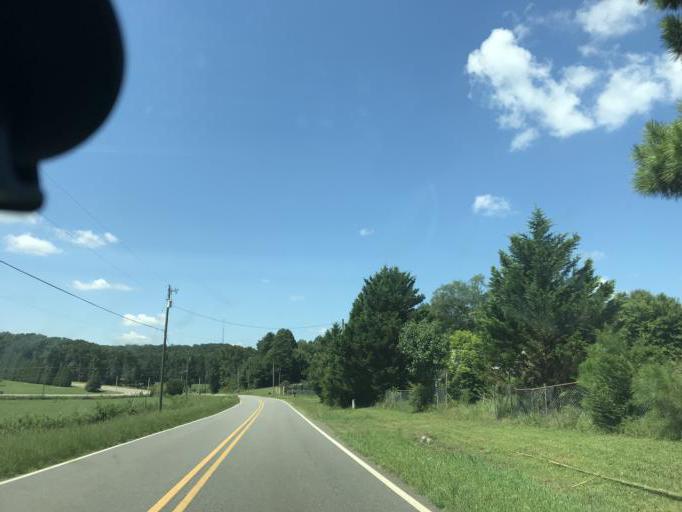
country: US
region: Georgia
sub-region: Dawson County
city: Dawsonville
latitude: 34.3104
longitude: -84.0268
